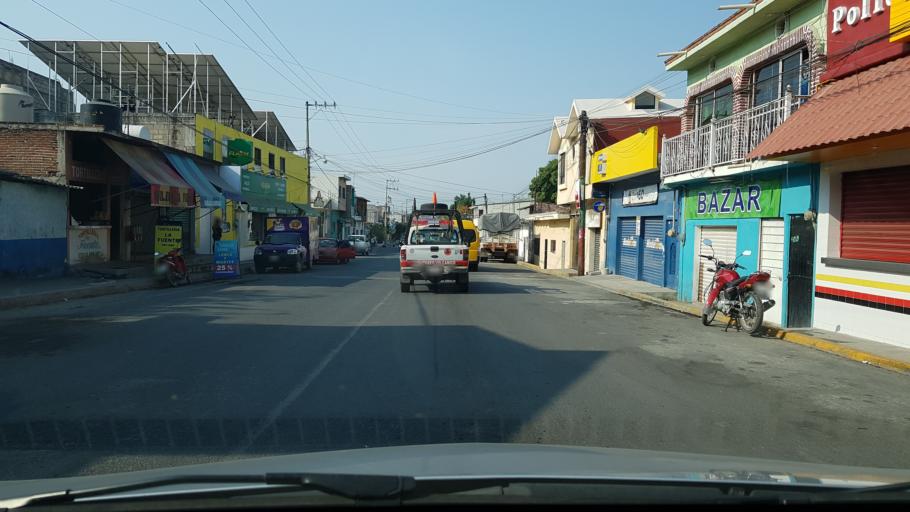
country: MX
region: Morelos
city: Tlaquiltenango
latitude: 18.6375
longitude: -99.1609
